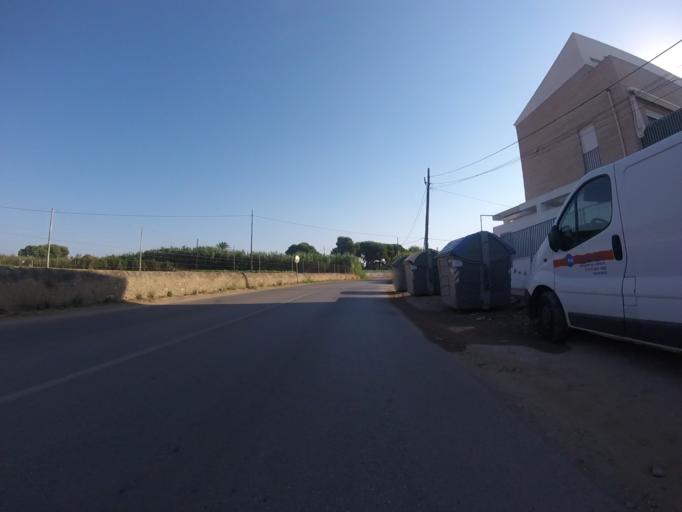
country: ES
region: Valencia
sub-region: Provincia de Castello
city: Benicarlo
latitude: 40.4033
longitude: 0.4143
